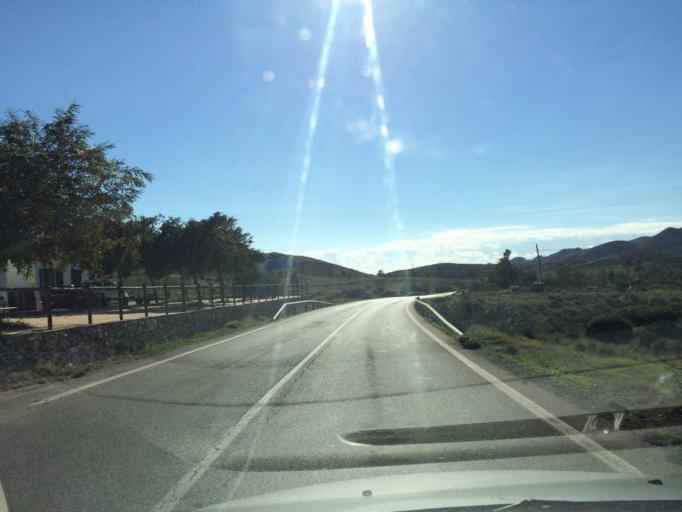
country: ES
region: Andalusia
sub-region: Provincia de Almeria
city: San Jose
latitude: 36.7884
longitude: -2.1092
